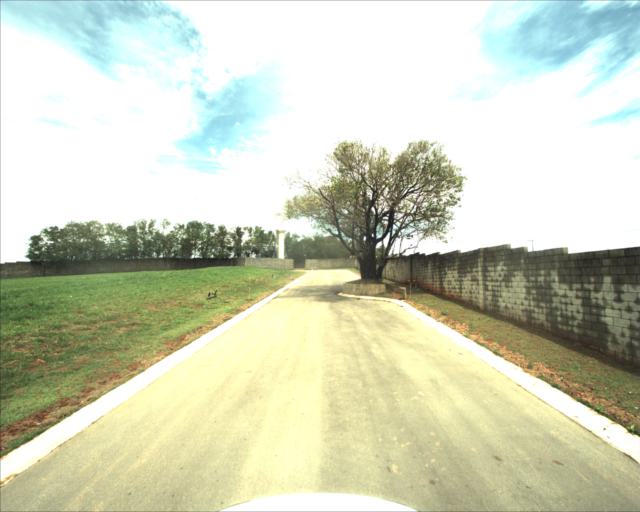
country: BR
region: Sao Paulo
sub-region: Votorantim
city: Votorantim
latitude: -23.5745
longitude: -47.5091
